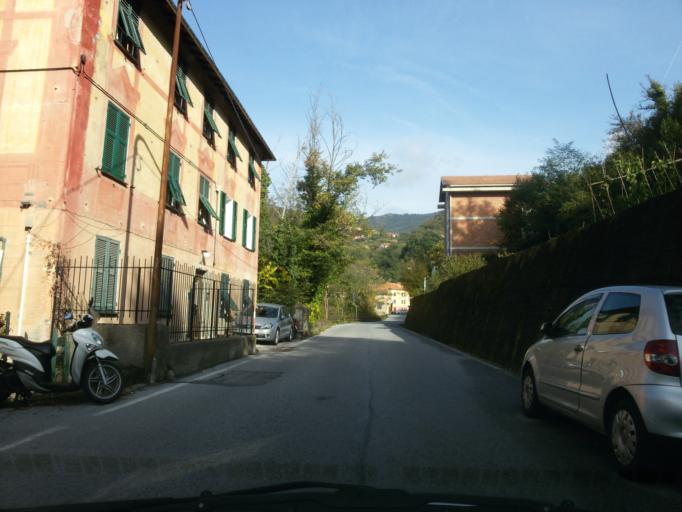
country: IT
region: Liguria
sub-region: Provincia di Genova
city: Piccarello
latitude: 44.4830
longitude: 8.9653
